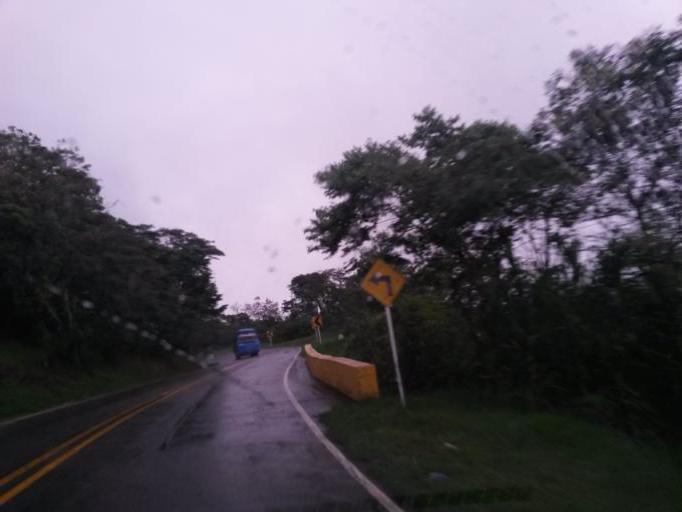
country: CO
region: Cauca
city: Popayan
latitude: 2.4069
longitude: -76.5079
